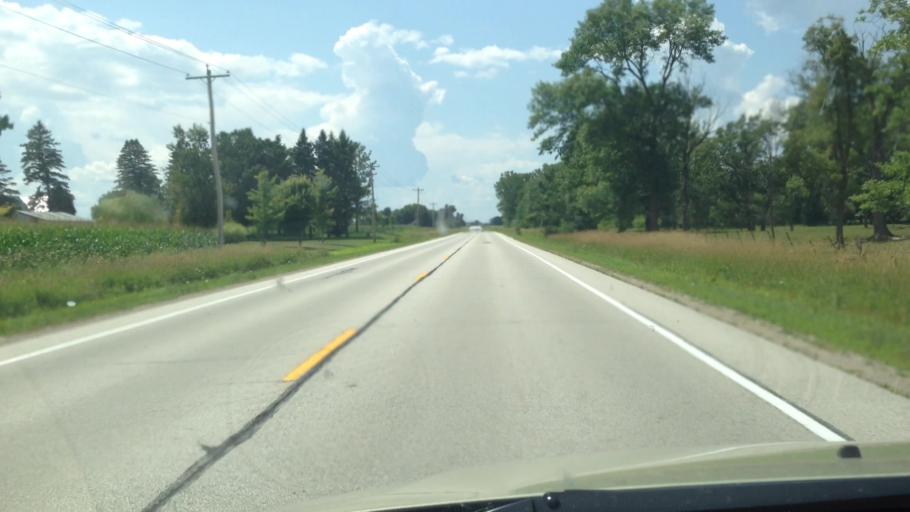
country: US
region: Wisconsin
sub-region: Brown County
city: Pulaski
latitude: 44.6583
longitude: -88.1981
